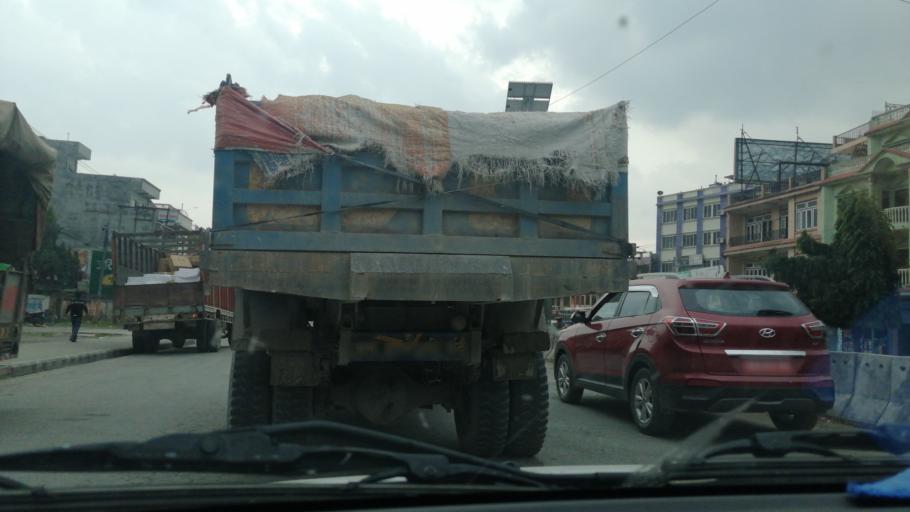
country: NP
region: Western Region
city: Butwal
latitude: 27.7053
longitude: 83.4672
